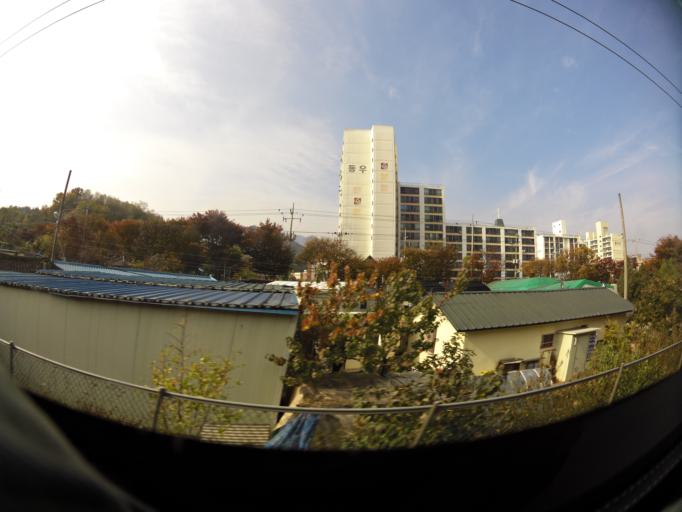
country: KR
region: Gyeongsangbuk-do
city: Gumi
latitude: 36.1082
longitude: 128.3577
